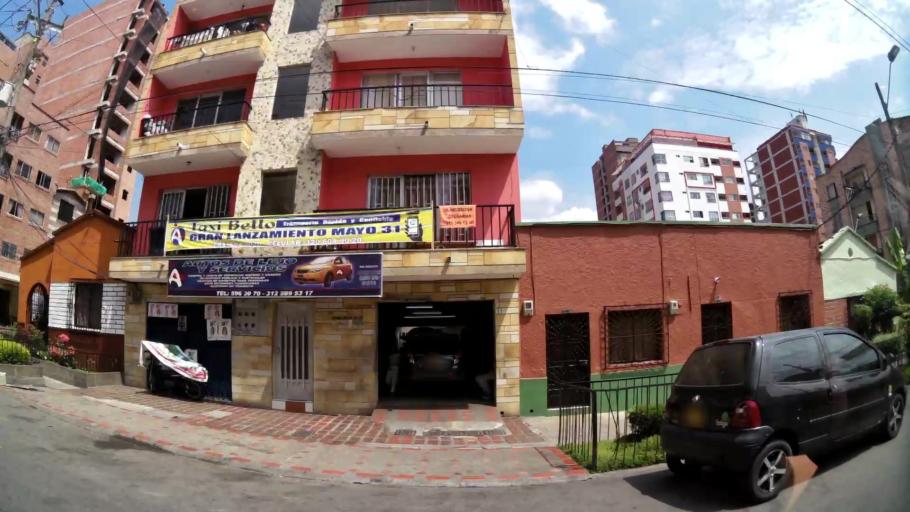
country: CO
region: Antioquia
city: Bello
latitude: 6.3225
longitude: -75.5599
